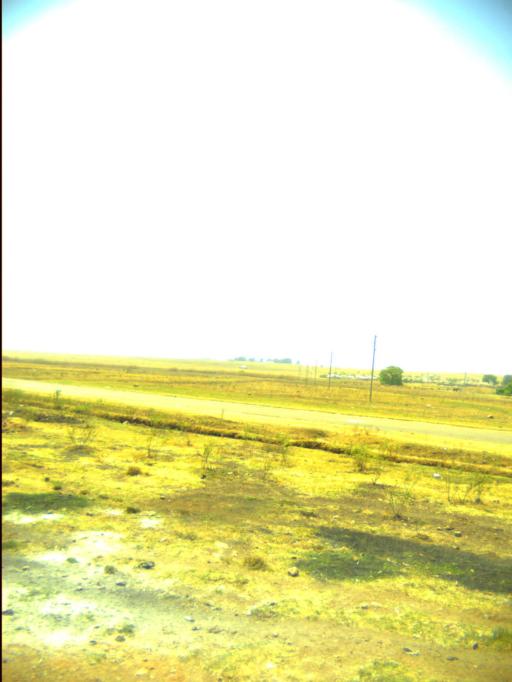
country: ZA
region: Mpumalanga
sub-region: Nkangala District Municipality
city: Delmas
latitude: -26.1380
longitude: 28.6982
